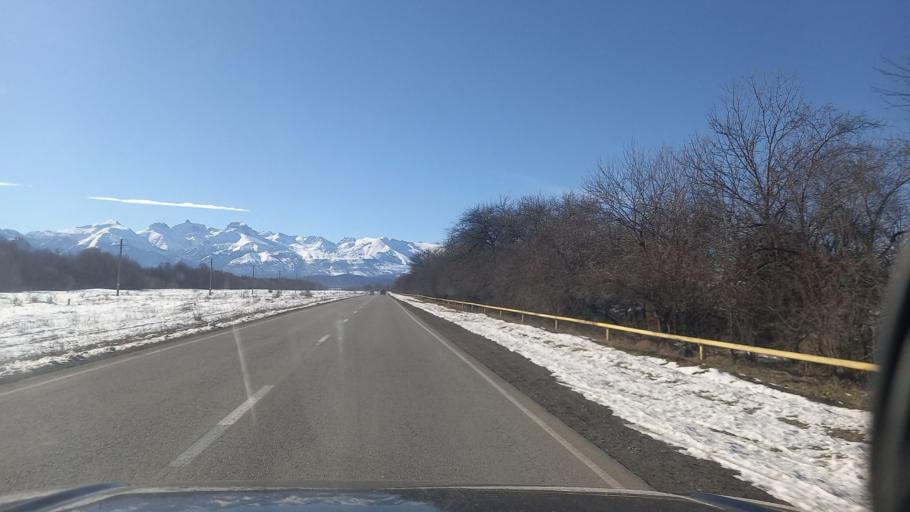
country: RU
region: North Ossetia
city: Chikola
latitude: 43.1787
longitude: 43.8841
